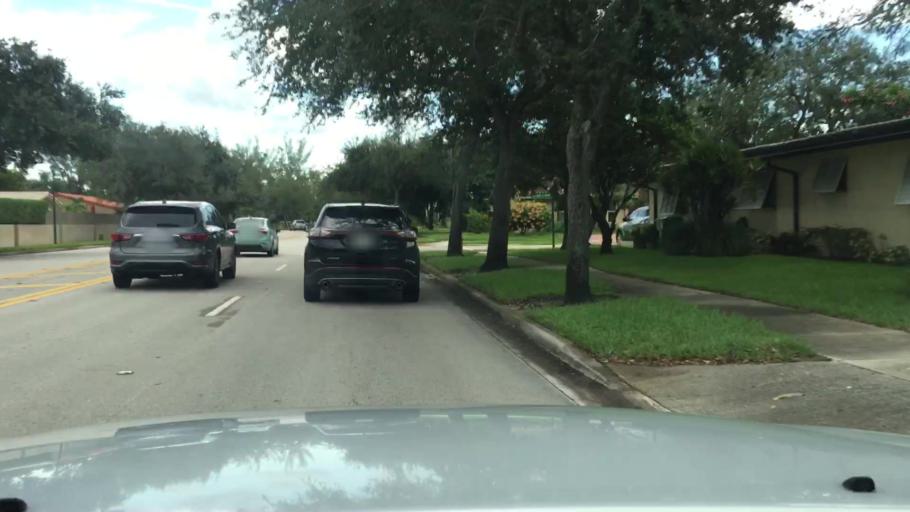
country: US
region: Florida
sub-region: Miami-Dade County
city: Miami Lakes
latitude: 25.9110
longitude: -80.3038
